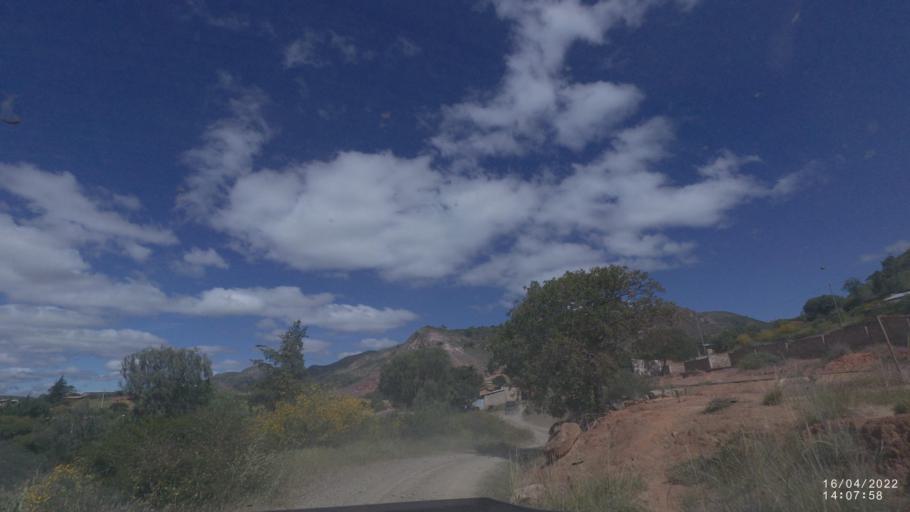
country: BO
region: Cochabamba
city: Mizque
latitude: -18.0594
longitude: -65.5243
